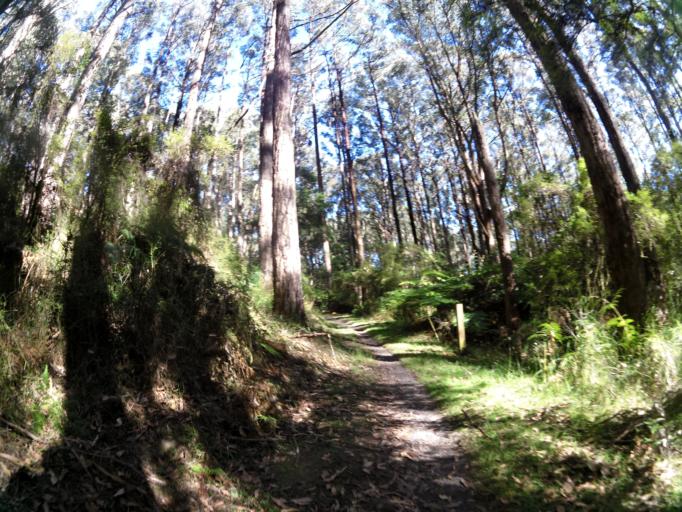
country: AU
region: Victoria
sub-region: Colac-Otway
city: Apollo Bay
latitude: -38.5475
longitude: 143.7417
